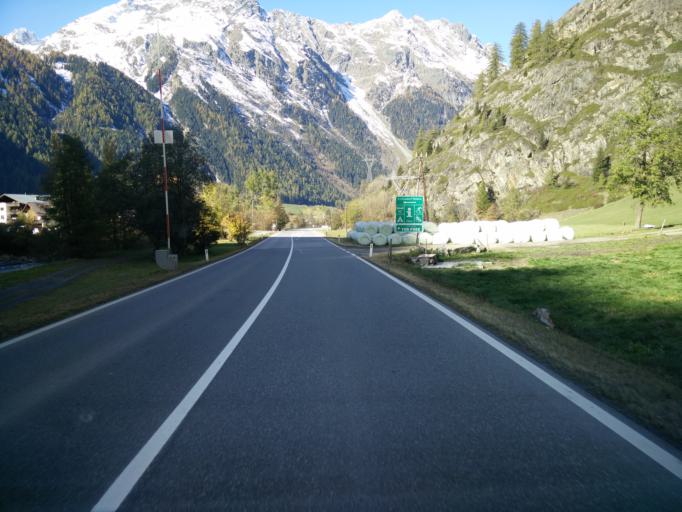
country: AT
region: Tyrol
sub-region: Politischer Bezirk Imst
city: Soelden
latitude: 47.0401
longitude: 10.9809
